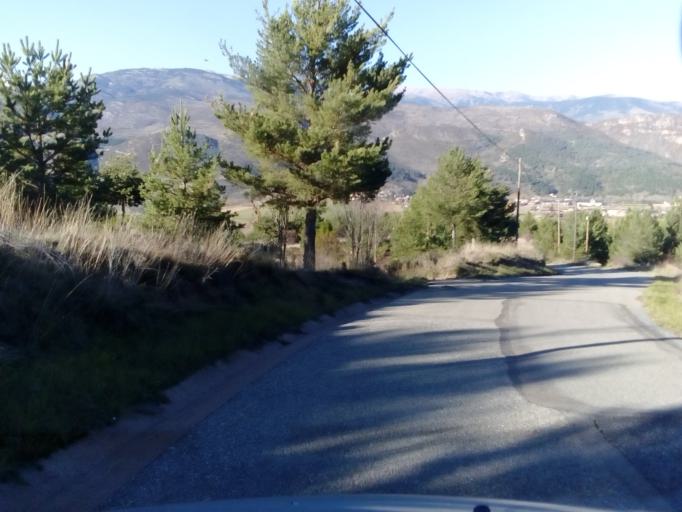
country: ES
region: Catalonia
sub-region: Provincia de Lleida
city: Bellver de Cerdanya
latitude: 42.3523
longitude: 1.7778
